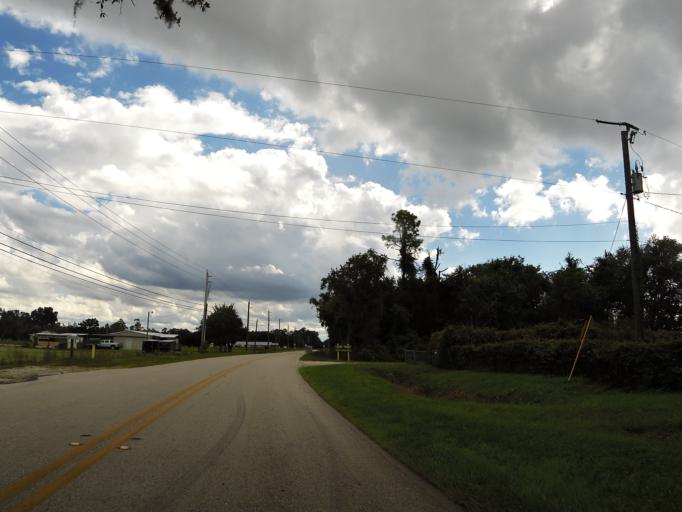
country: US
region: Florida
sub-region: Saint Johns County
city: Saint Augustine South
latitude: 29.8464
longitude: -81.4986
